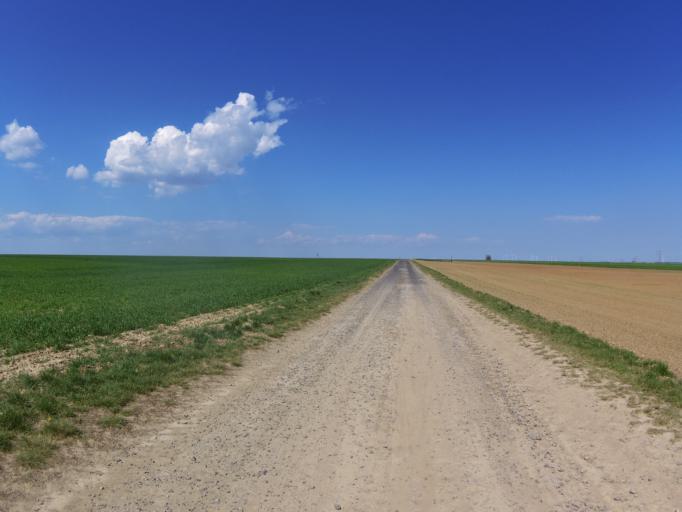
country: DE
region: Bavaria
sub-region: Regierungsbezirk Unterfranken
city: Oberpleichfeld
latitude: 49.8495
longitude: 10.0877
